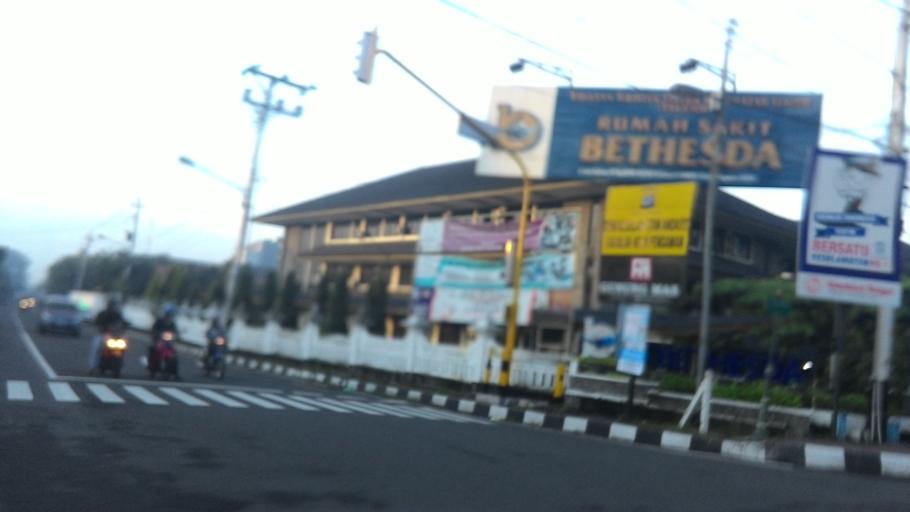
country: ID
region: Daerah Istimewa Yogyakarta
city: Yogyakarta
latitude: -7.7830
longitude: 110.3793
